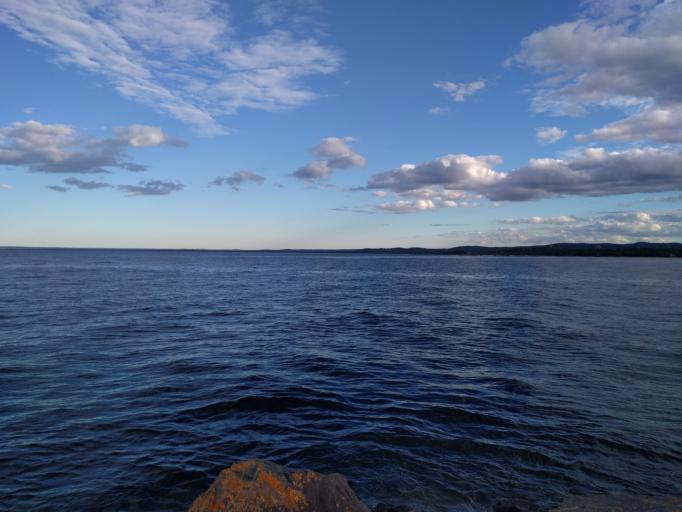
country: US
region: Michigan
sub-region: Marquette County
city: Marquette
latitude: 46.5741
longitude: -87.3744
